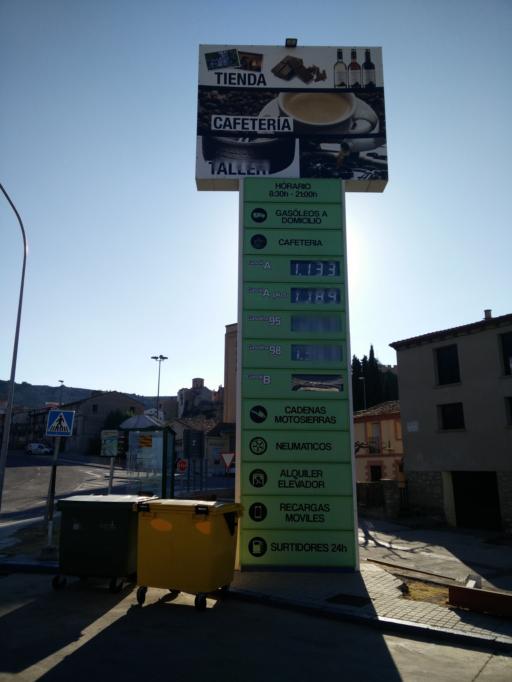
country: ES
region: Aragon
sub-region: Provincia de Zaragoza
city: Nuevalos
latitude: 41.2128
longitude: -1.7882
